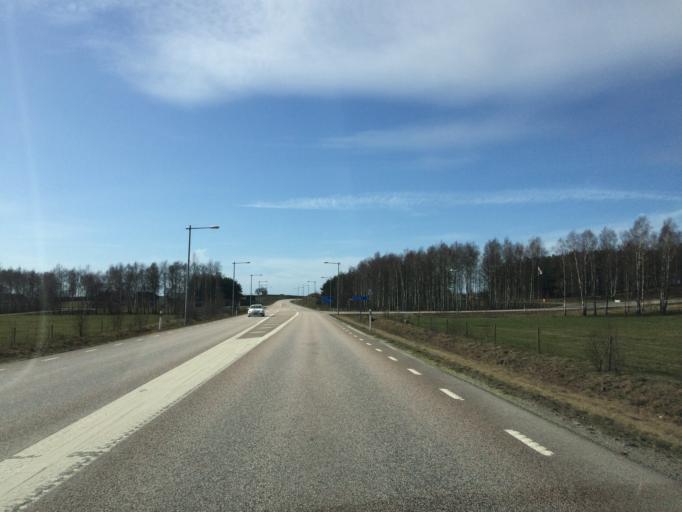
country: SE
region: Halland
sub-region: Laholms Kommun
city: Veinge
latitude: 56.5439
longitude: 13.0734
